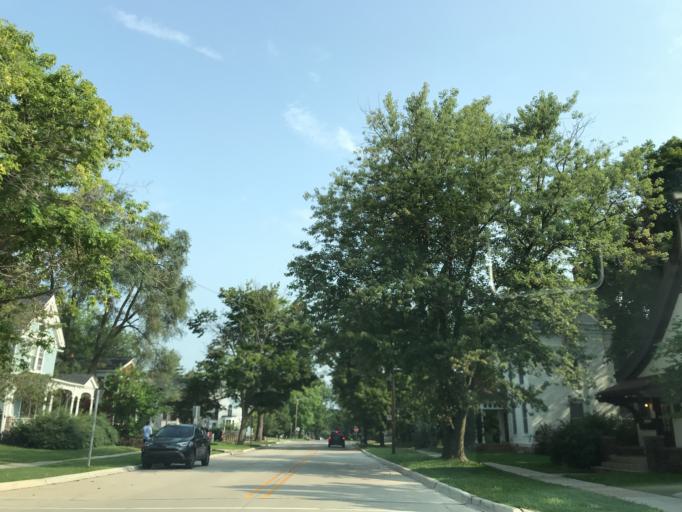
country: US
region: Michigan
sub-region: Washtenaw County
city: Ypsilanti
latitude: 42.2445
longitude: -83.6160
